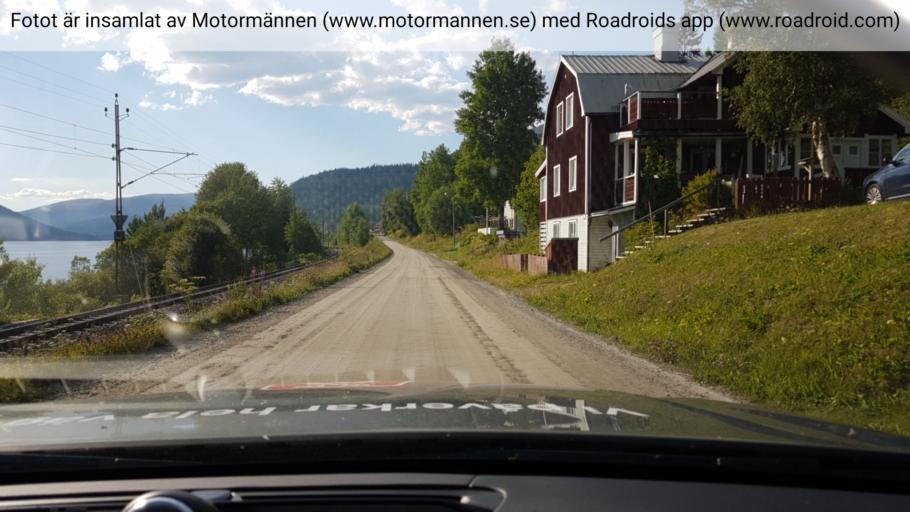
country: SE
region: Jaemtland
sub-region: Are Kommun
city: Are
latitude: 63.3802
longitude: 13.1418
